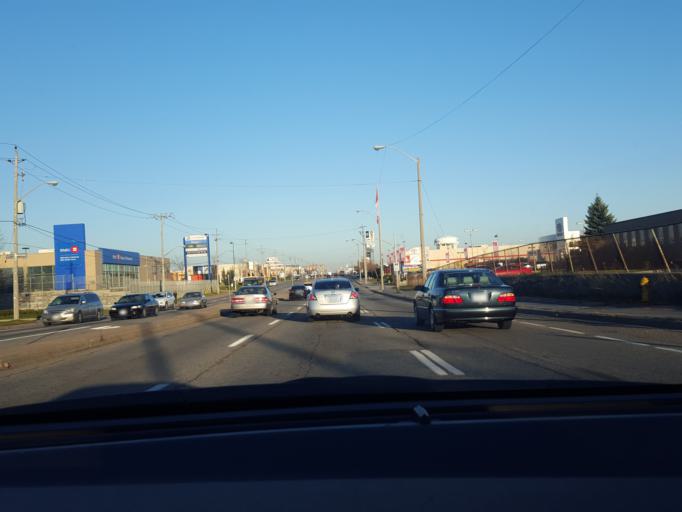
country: CA
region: Ontario
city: Scarborough
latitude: 43.7257
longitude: -79.2970
